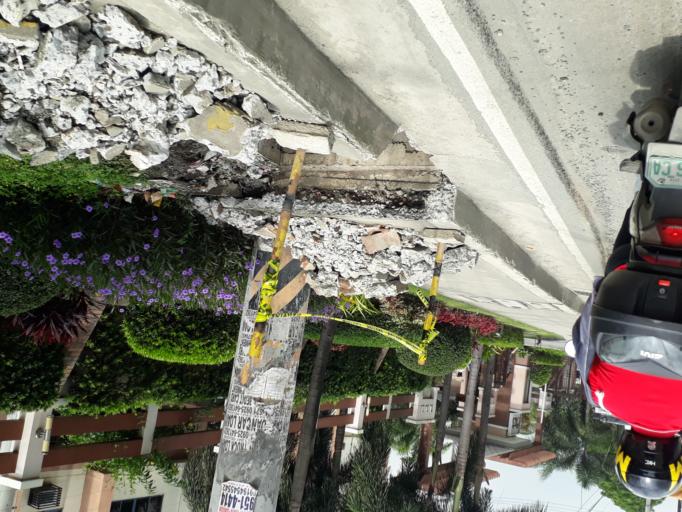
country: PH
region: Calabarzon
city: Bagong Pagasa
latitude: 14.6794
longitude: 121.0238
